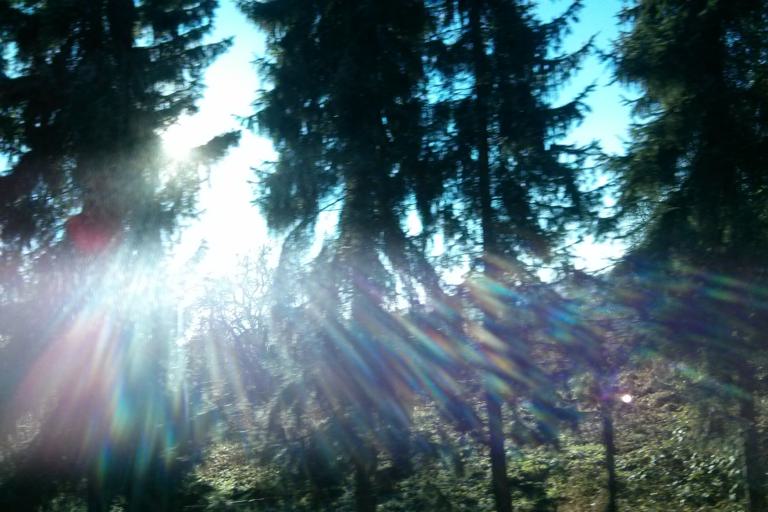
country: DE
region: North Rhine-Westphalia
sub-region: Regierungsbezirk Koln
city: Hennef
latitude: 50.7652
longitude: 7.3170
